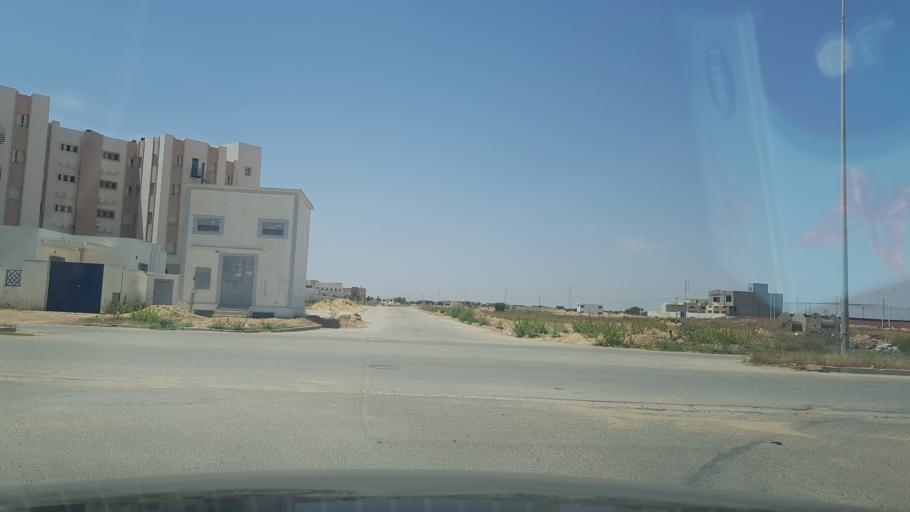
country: TN
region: Safaqis
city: Al Qarmadah
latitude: 34.8415
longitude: 10.7568
